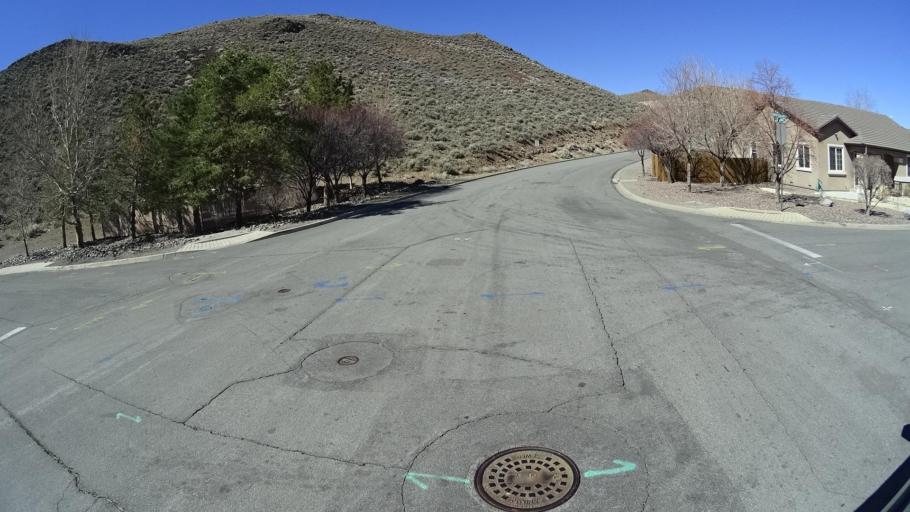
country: US
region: Nevada
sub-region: Washoe County
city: Sparks
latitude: 39.4767
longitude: -119.7234
